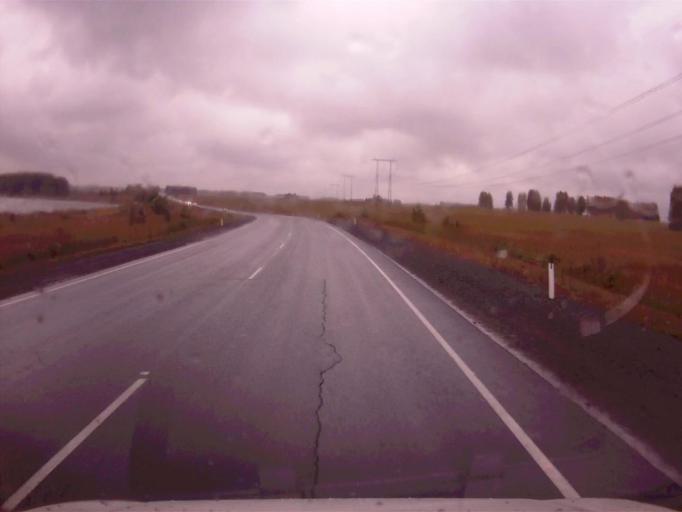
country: RU
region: Chelyabinsk
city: Roshchino
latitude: 55.3914
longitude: 61.1216
